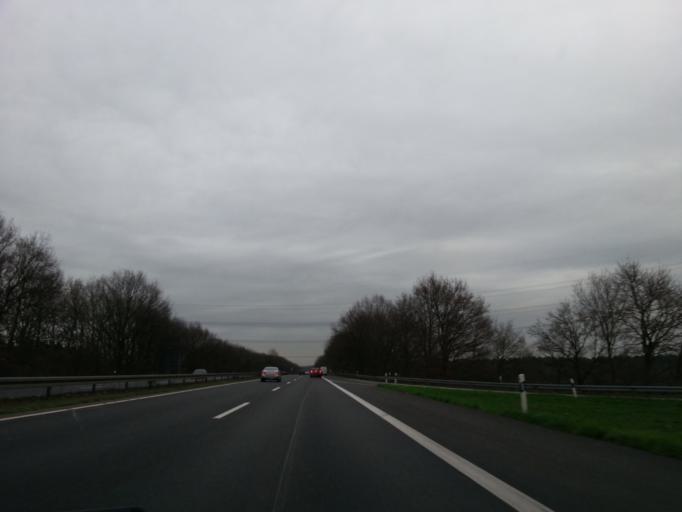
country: DE
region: North Rhine-Westphalia
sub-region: Regierungsbezirk Dusseldorf
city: Hunxe
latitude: 51.6654
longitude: 6.7213
